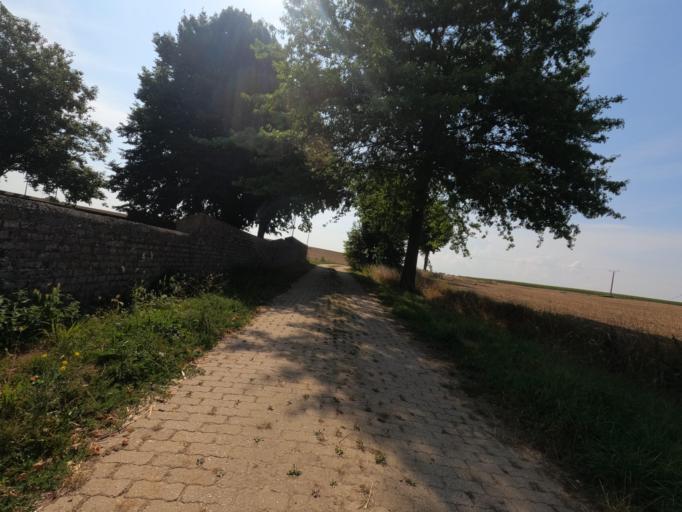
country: DE
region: North Rhine-Westphalia
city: Julich
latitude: 50.9810
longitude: 6.3666
